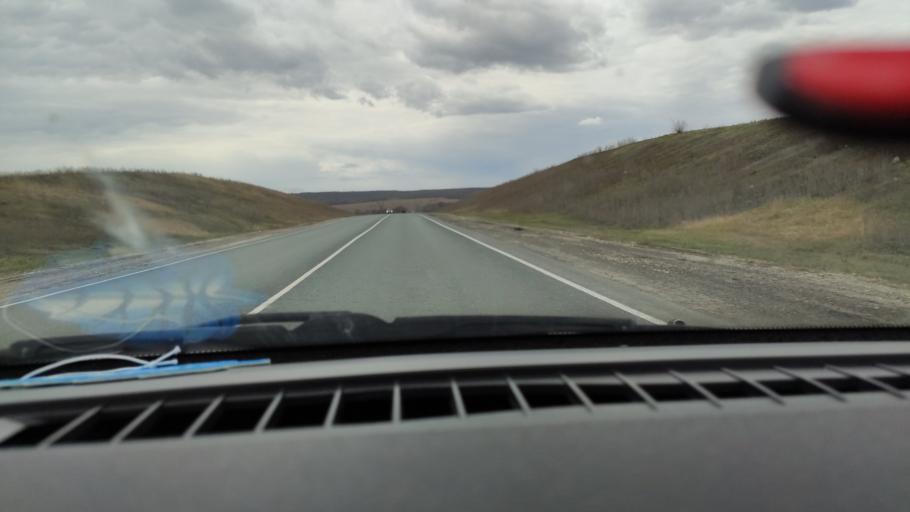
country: RU
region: Saratov
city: Sinodskoye
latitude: 51.9246
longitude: 46.5640
